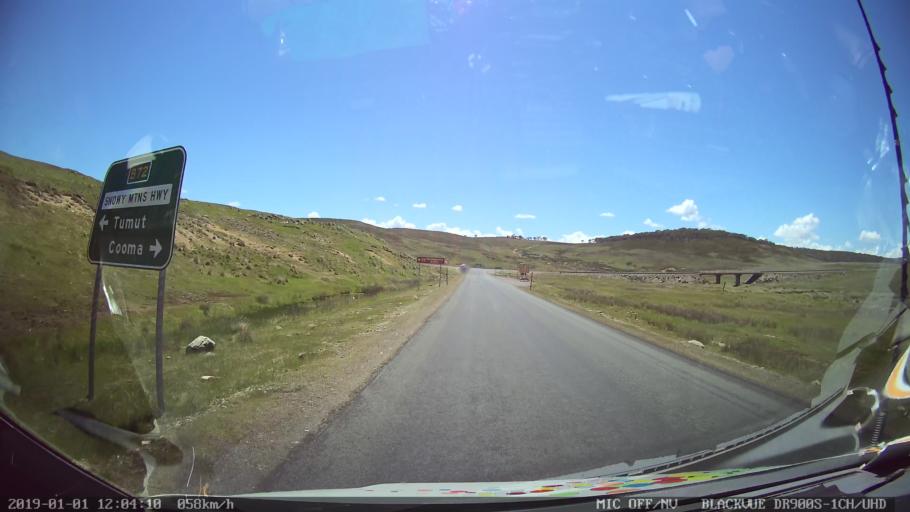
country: AU
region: New South Wales
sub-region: Snowy River
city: Jindabyne
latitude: -35.8679
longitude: 148.4938
